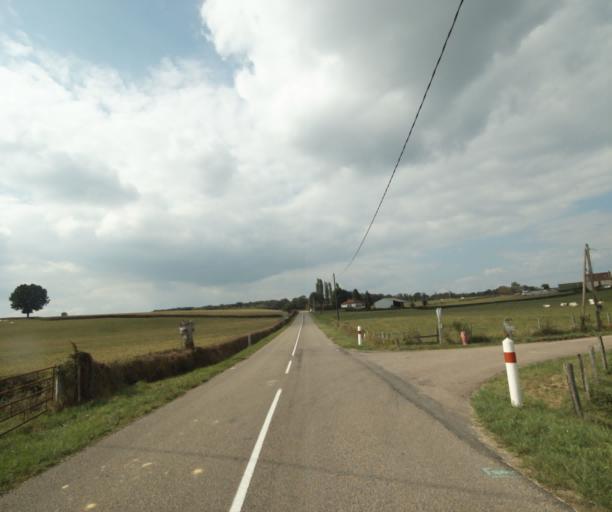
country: FR
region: Bourgogne
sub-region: Departement de Saone-et-Loire
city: Palinges
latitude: 46.5094
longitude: 4.1815
